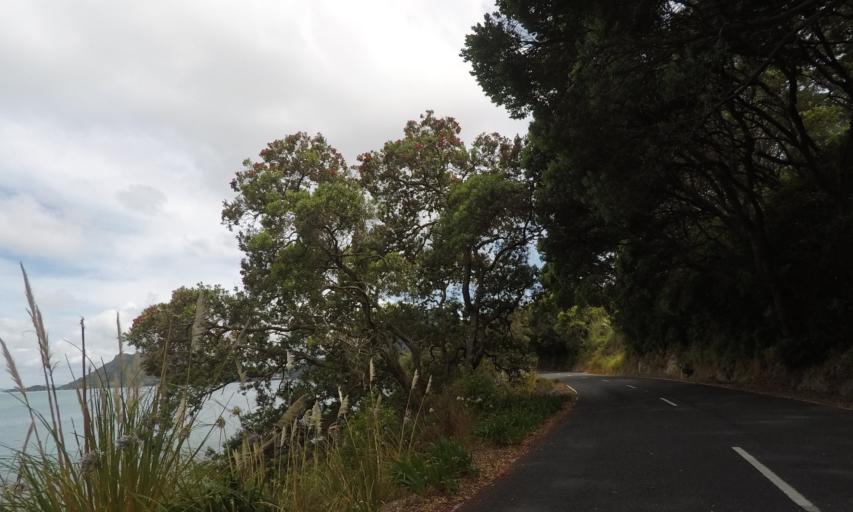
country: NZ
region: Northland
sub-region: Whangarei
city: Ruakaka
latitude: -35.8385
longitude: 174.5340
